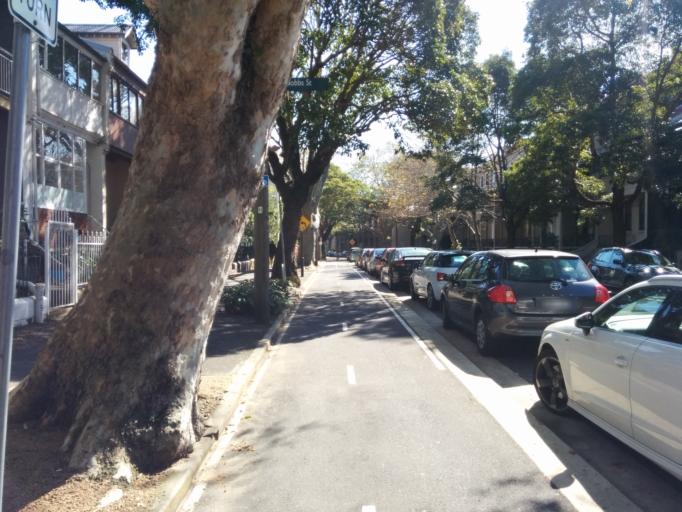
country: AU
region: New South Wales
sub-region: City of Sydney
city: Darlinghurst
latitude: -33.8891
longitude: 151.2151
